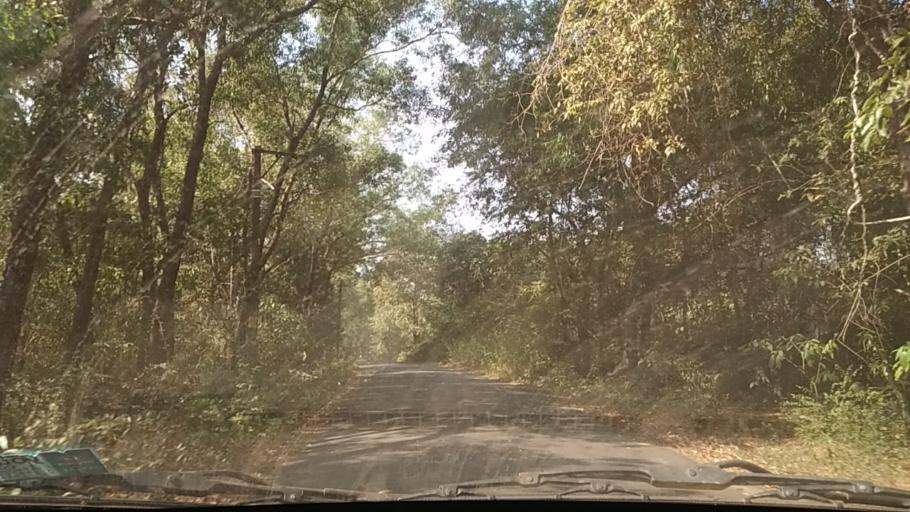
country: IN
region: Goa
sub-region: North Goa
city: Ponda
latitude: 15.3665
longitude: 74.0892
